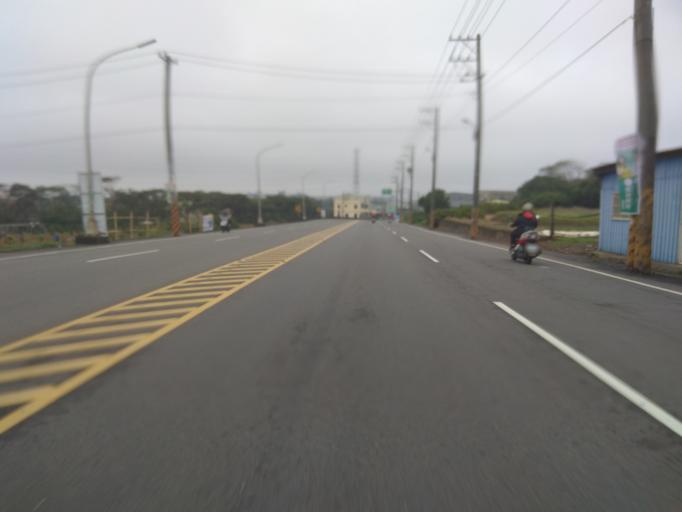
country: TW
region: Taiwan
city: Taoyuan City
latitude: 25.0175
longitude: 121.1260
